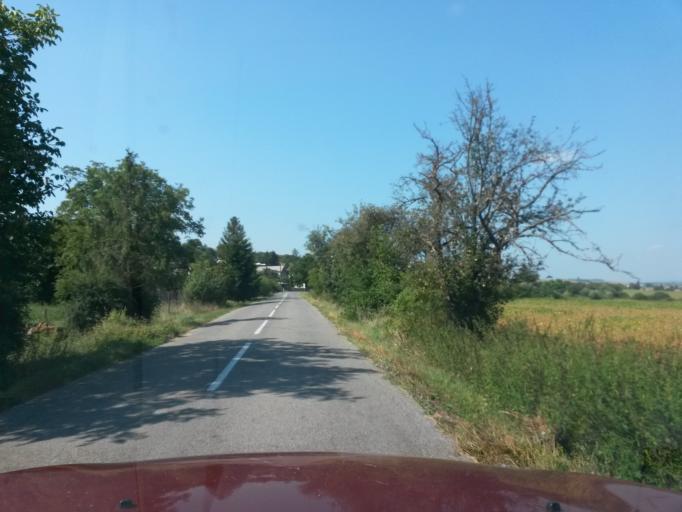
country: SK
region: Kosicky
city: Moldava nad Bodvou
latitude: 48.5314
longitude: 21.1282
